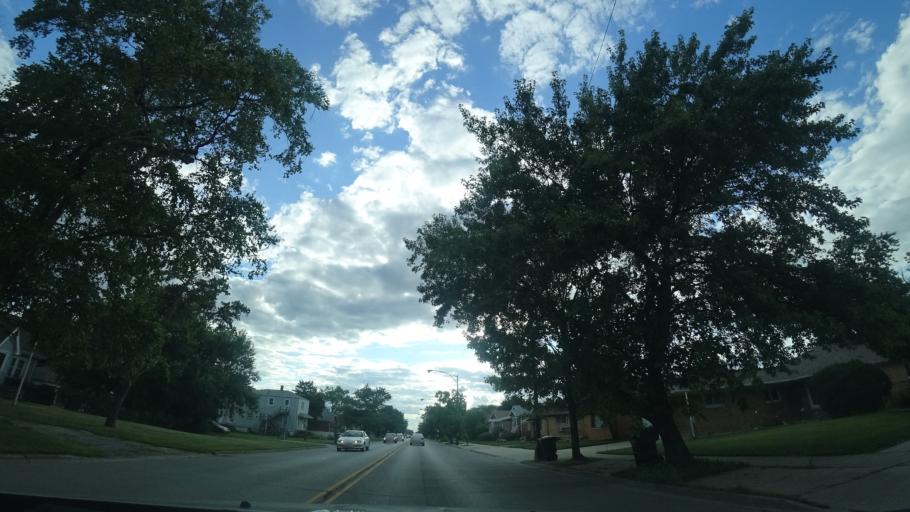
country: US
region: Illinois
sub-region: Cook County
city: Merrionette Park
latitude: 41.6841
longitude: -87.7135
